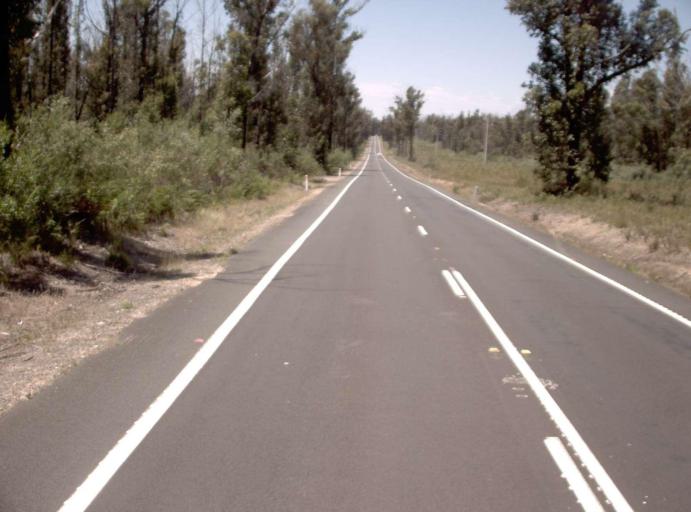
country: AU
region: Victoria
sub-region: East Gippsland
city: Lakes Entrance
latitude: -37.7514
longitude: 148.2458
